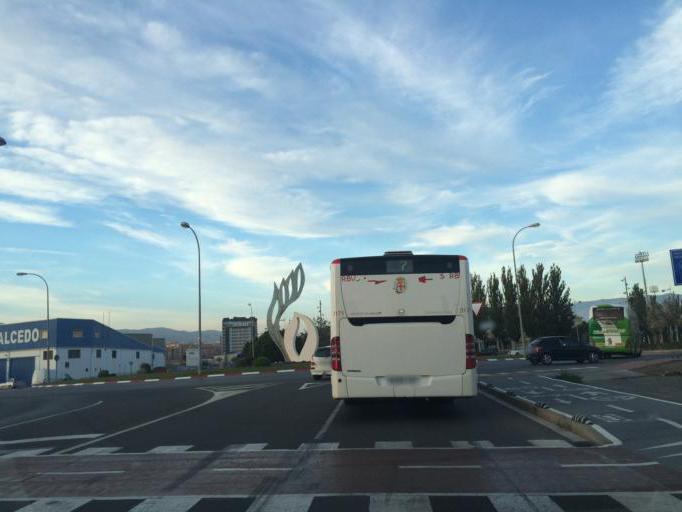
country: ES
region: Andalusia
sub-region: Provincia de Almeria
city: Almeria
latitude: 36.8362
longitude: -2.4385
